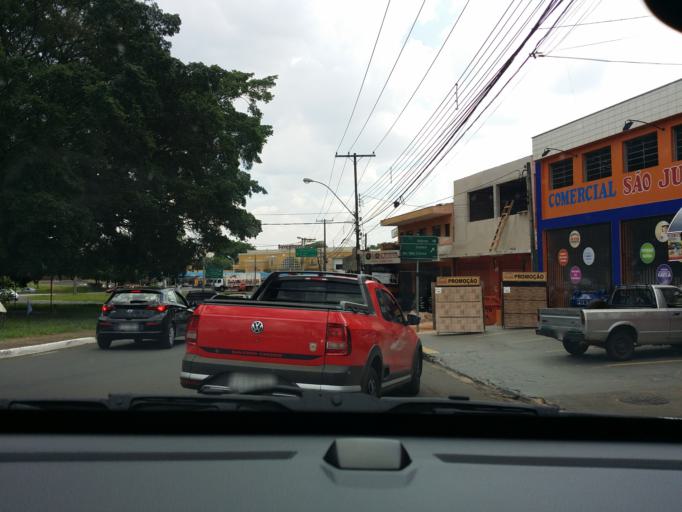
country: BR
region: Sao Paulo
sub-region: Sao Carlos
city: Sao Carlos
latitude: -22.0322
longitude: -47.8895
